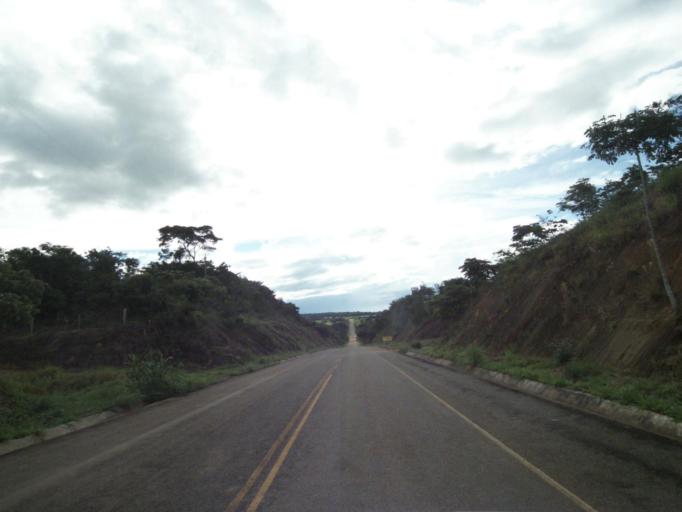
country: BR
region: Goias
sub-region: Jaragua
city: Jaragua
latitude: -15.8426
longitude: -49.3404
